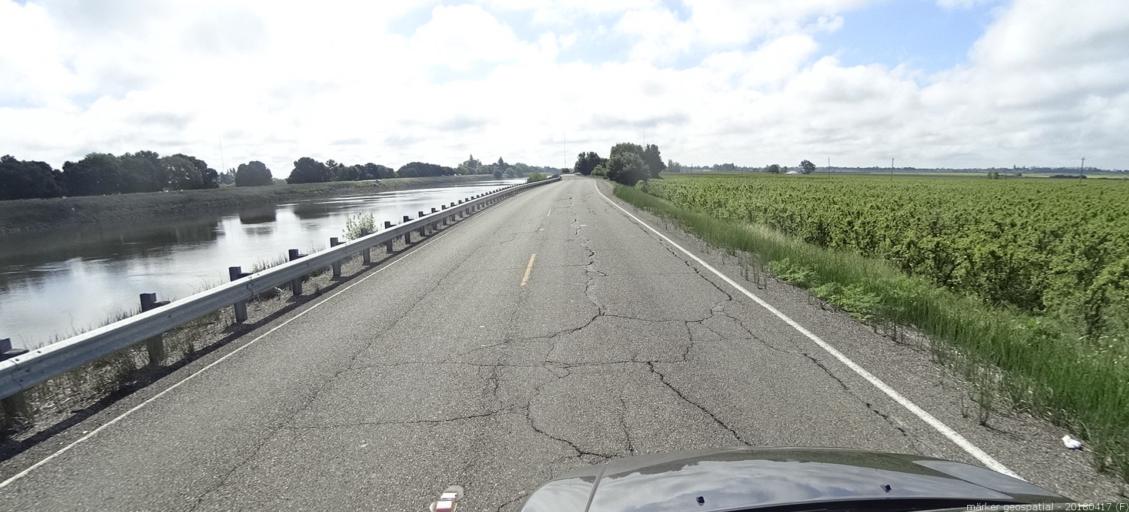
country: US
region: California
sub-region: Sacramento County
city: Walnut Grove
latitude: 38.2695
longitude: -121.5343
